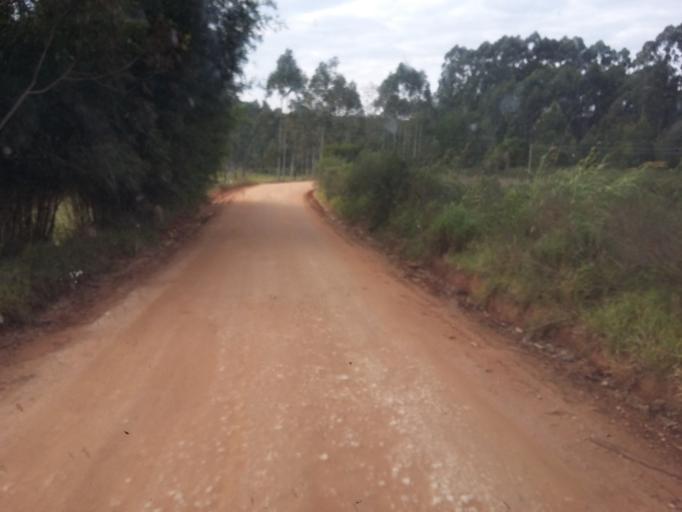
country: BR
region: Rio Grande do Sul
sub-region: Camaqua
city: Camaqua
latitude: -30.7175
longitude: -51.7832
